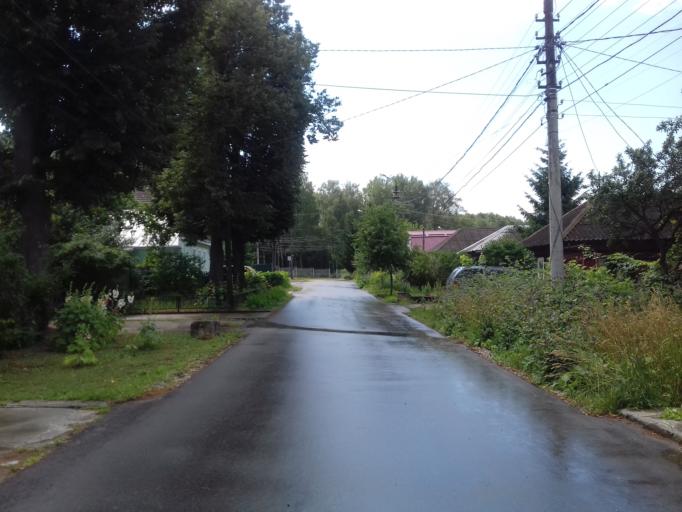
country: RU
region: Tula
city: Tula
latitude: 54.1869
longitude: 37.5813
